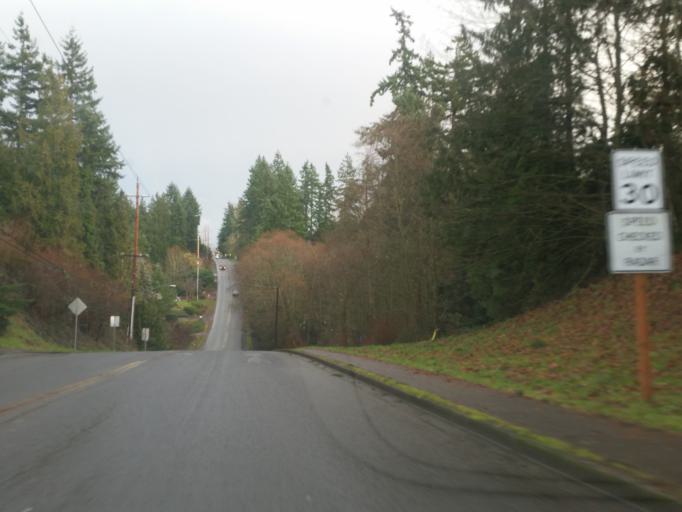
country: US
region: Washington
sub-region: Snohomish County
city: Brier
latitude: 47.7918
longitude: -122.2854
